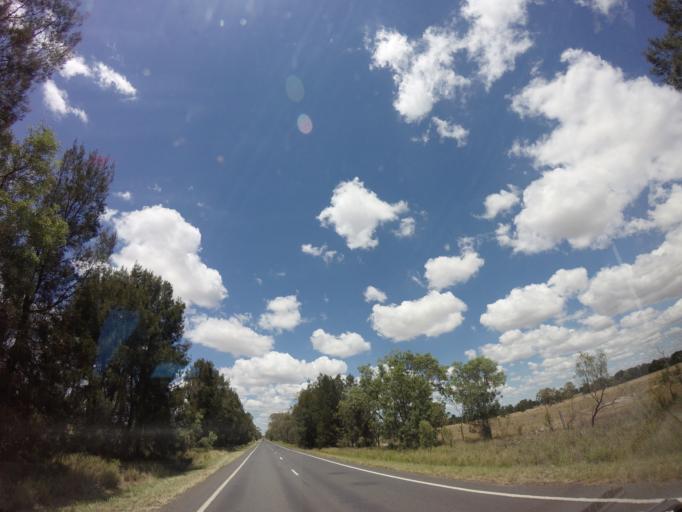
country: AU
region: Queensland
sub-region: Toowoomba
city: Oakey
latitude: -27.8916
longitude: 151.2127
